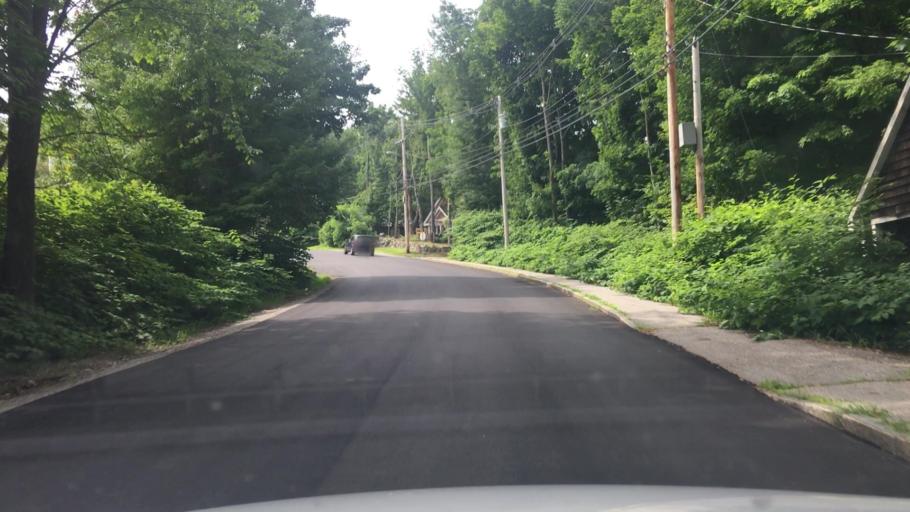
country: US
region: New Hampshire
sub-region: Belknap County
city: Meredith
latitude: 43.6491
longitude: -71.5011
